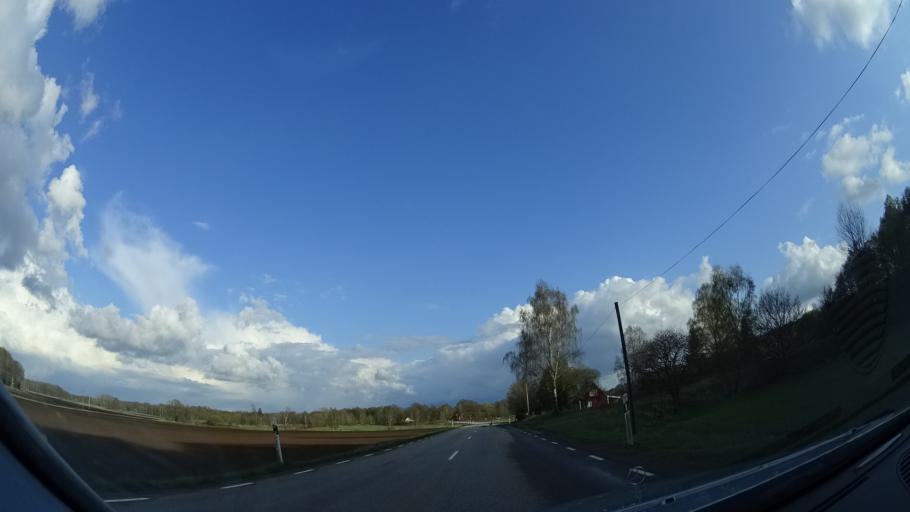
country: SE
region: Skane
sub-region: Klippans Kommun
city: Ljungbyhed
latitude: 56.0261
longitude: 13.2675
